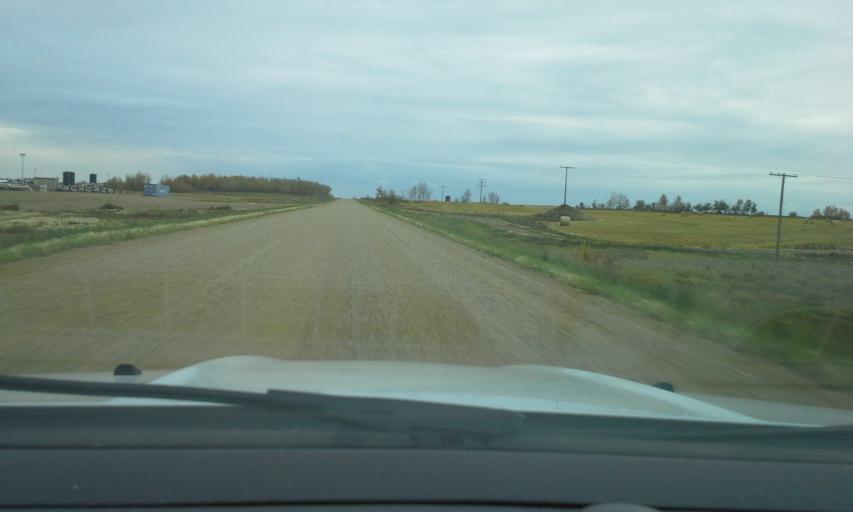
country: CA
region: Saskatchewan
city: Lloydminster
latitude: 53.2815
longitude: -109.8084
